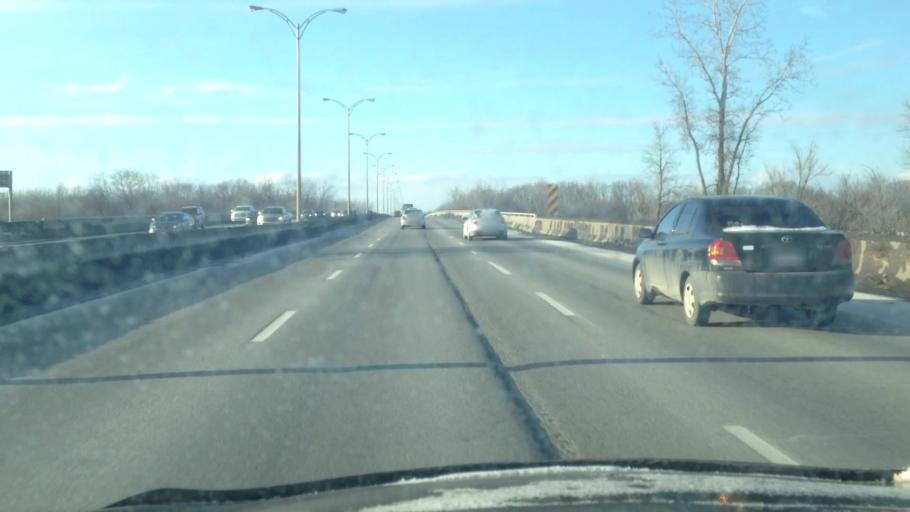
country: CA
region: Quebec
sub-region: Laurentides
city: Boisbriand
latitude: 45.6083
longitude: -73.8104
